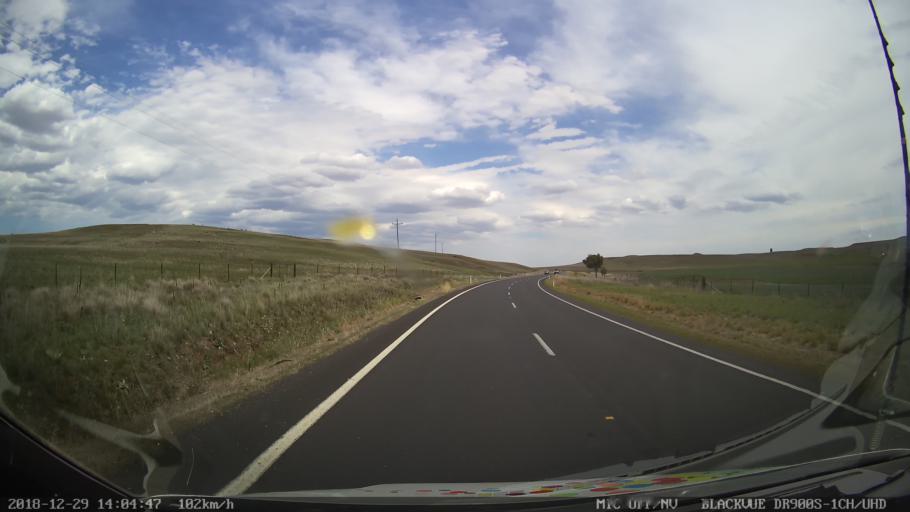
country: AU
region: New South Wales
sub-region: Cooma-Monaro
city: Cooma
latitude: -36.3212
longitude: 149.1886
